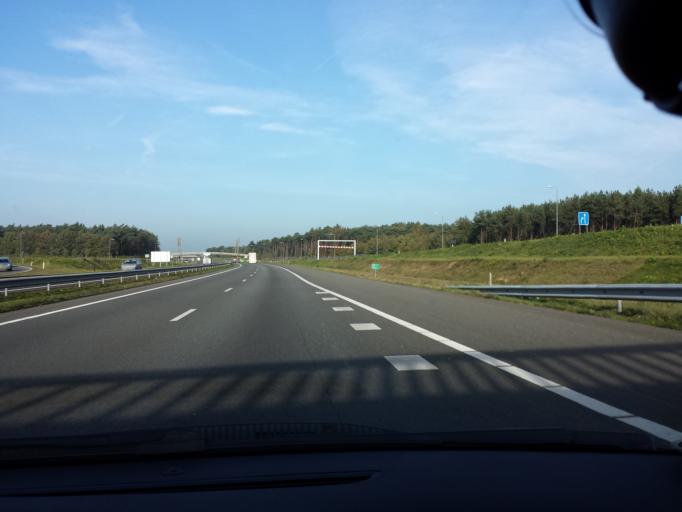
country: NL
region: Limburg
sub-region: Gemeente Venlo
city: Venlo
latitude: 51.4141
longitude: 6.1229
